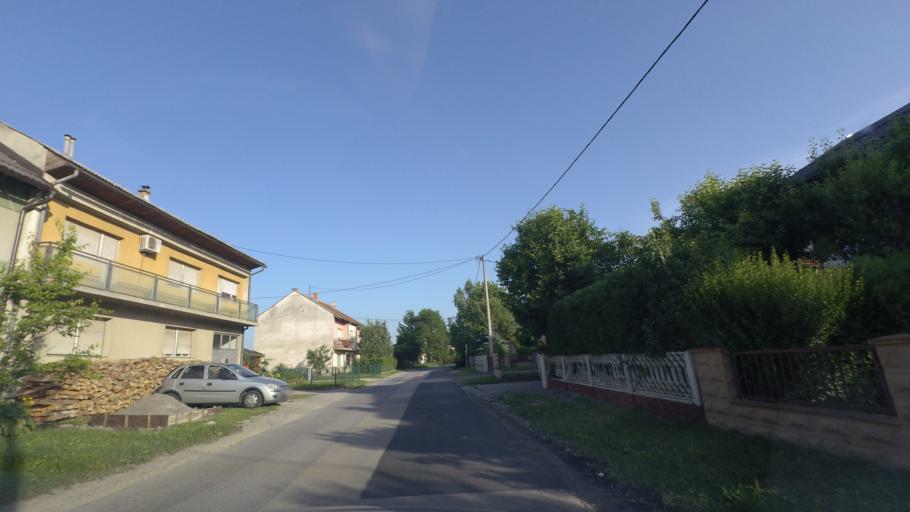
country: HR
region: Karlovacka
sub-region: Grad Karlovac
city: Karlovac
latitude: 45.5040
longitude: 15.5320
